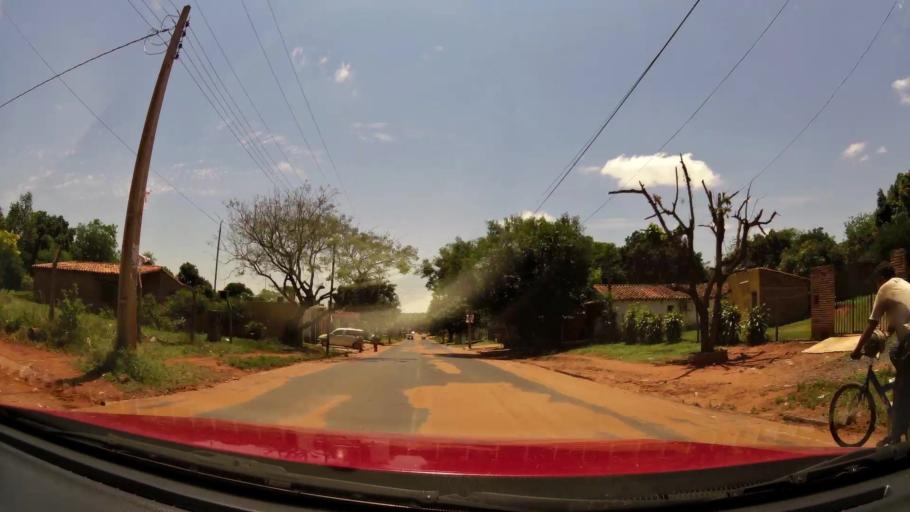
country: PY
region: Central
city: Nemby
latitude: -25.4128
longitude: -57.5250
